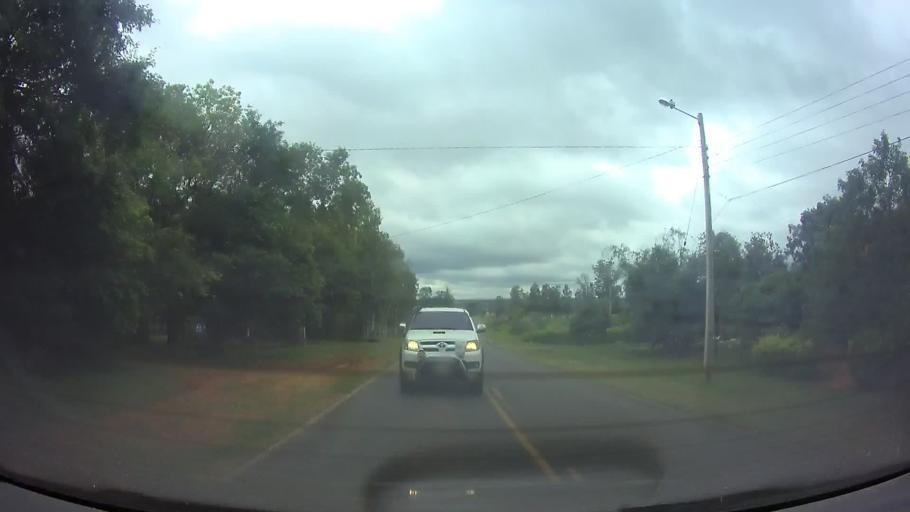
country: PY
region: Central
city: Guarambare
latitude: -25.5108
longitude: -57.4879
